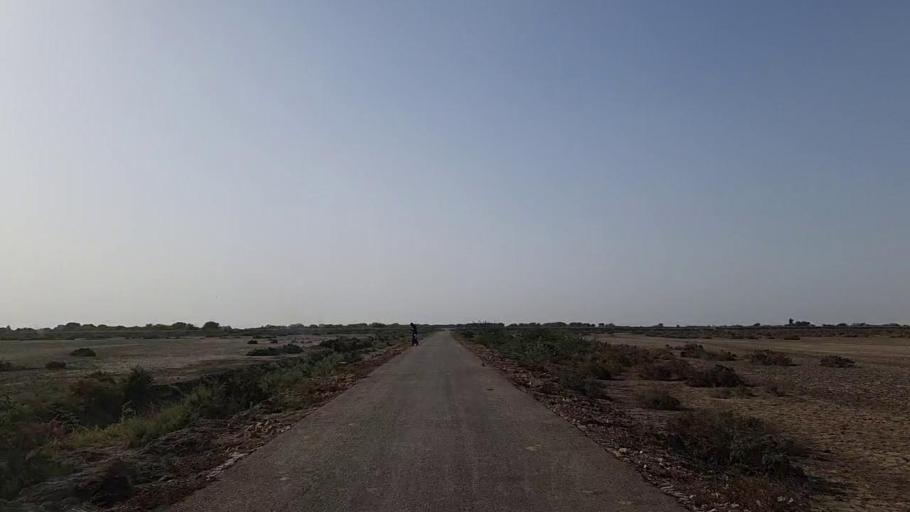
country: PK
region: Sindh
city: Jati
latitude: 24.3028
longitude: 68.1976
